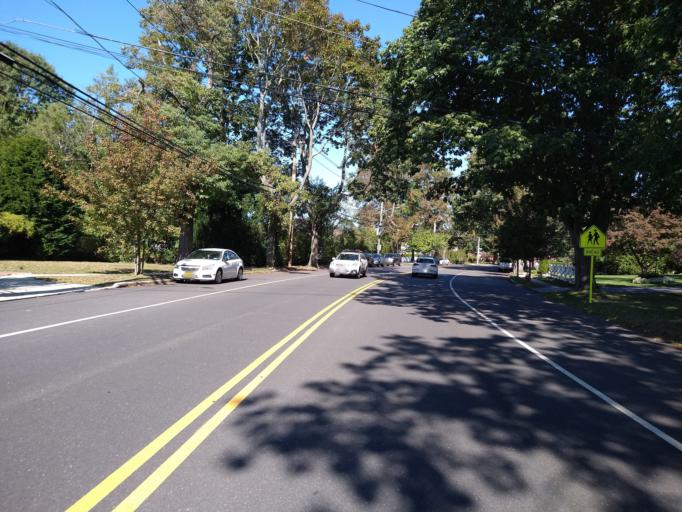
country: US
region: New York
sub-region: Nassau County
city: Syosset
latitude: 40.8312
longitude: -73.4941
